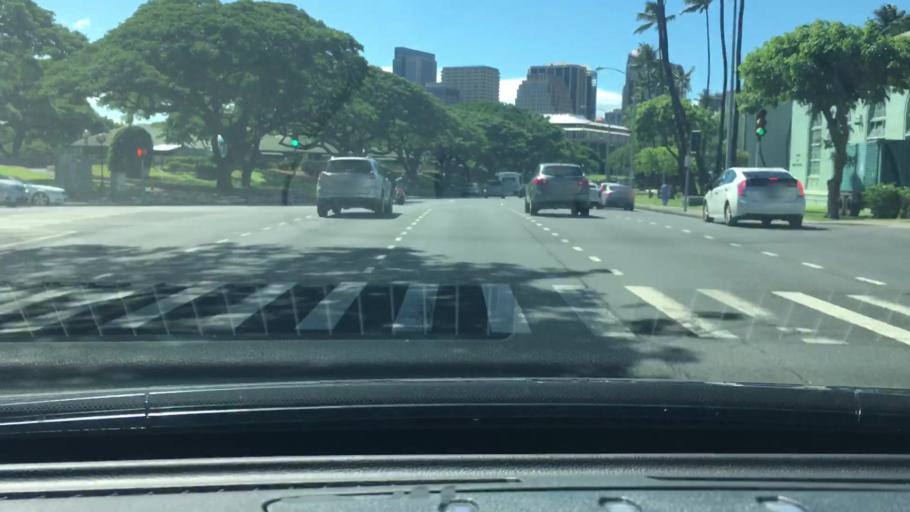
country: US
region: Hawaii
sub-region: Honolulu County
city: Honolulu
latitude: 21.3050
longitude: -157.8525
